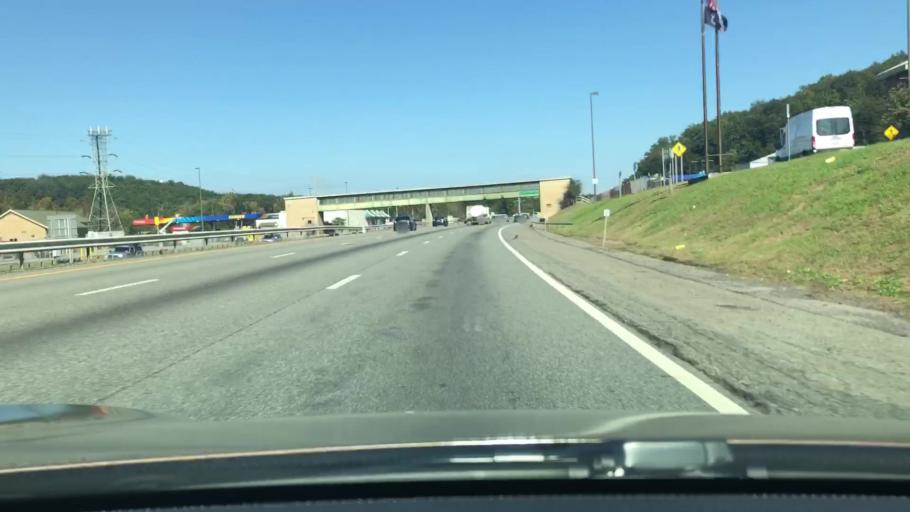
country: US
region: New York
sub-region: Rockland County
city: Sloatsburg
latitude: 41.1509
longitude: -74.1888
